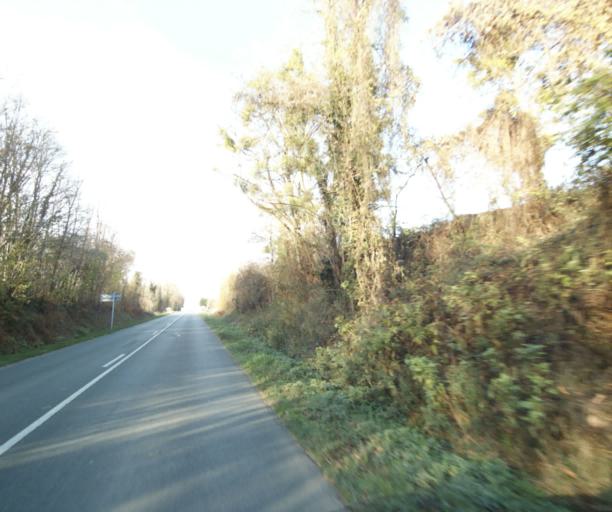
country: FR
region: Poitou-Charentes
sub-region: Departement de la Charente-Maritime
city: Burie
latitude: 45.7990
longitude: -0.4441
